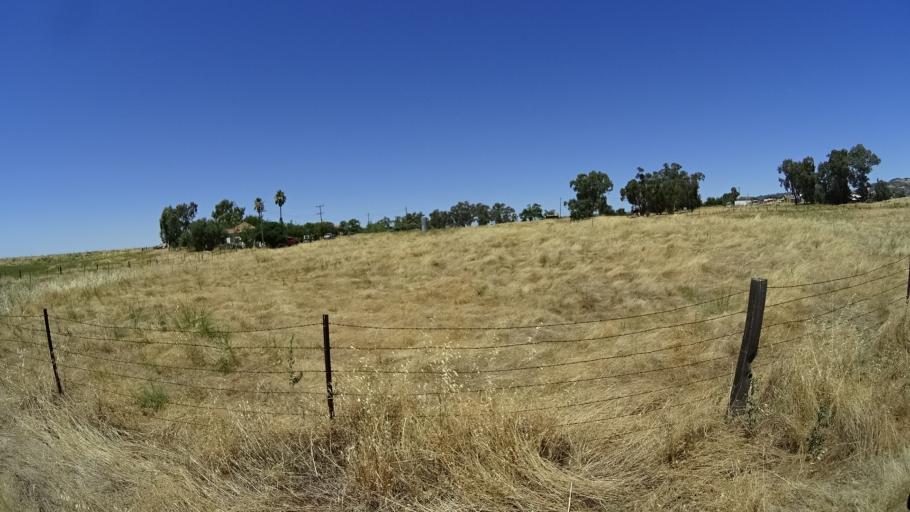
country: US
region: California
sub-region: Calaveras County
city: Rancho Calaveras
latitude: 38.0297
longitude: -120.8547
